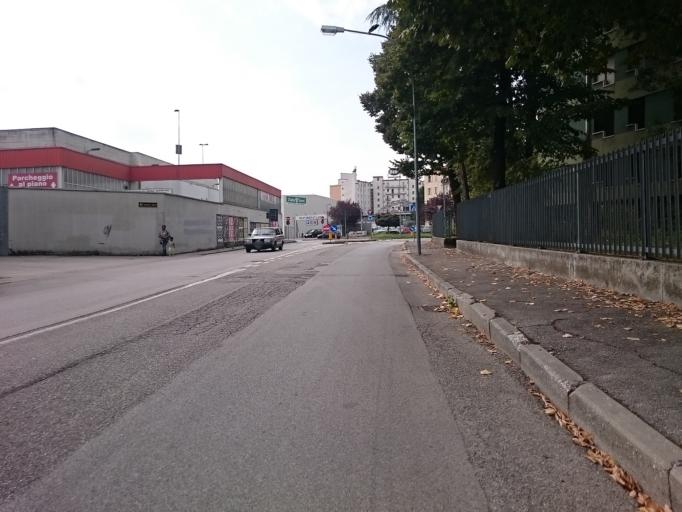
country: IT
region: Veneto
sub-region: Provincia di Padova
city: Padova
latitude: 45.4111
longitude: 11.9047
